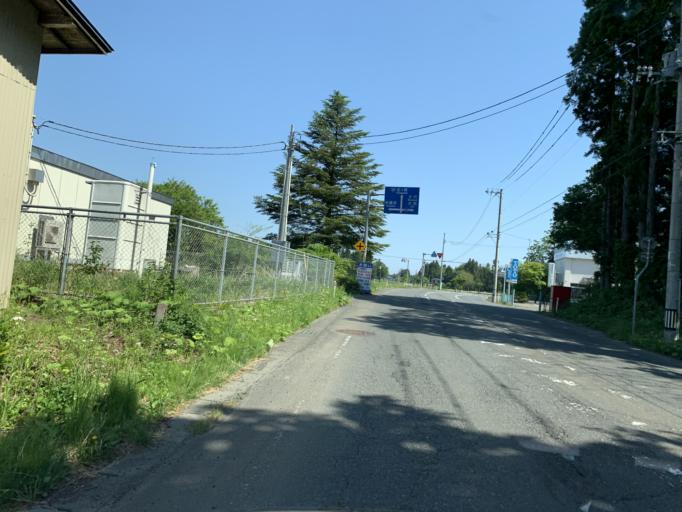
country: JP
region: Iwate
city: Mizusawa
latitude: 39.1014
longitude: 141.0759
